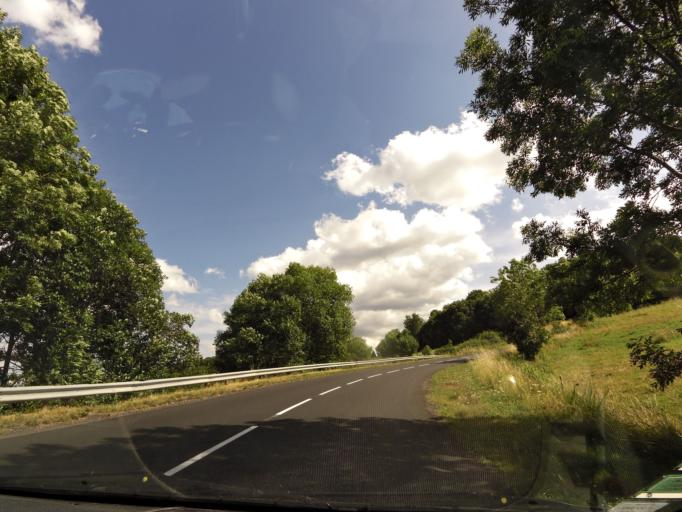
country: FR
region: Auvergne
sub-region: Departement du Puy-de-Dome
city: Aydat
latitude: 45.5578
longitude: 2.9486
